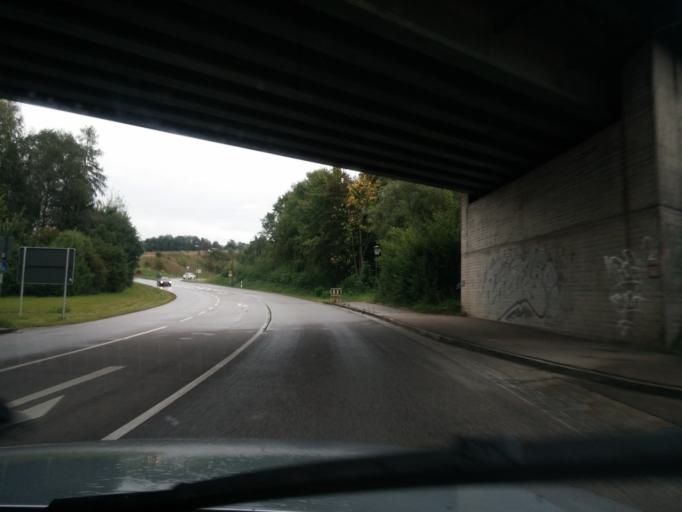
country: DE
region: Bavaria
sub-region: Upper Bavaria
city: Reichertshausen
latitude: 48.4646
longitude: 11.5091
